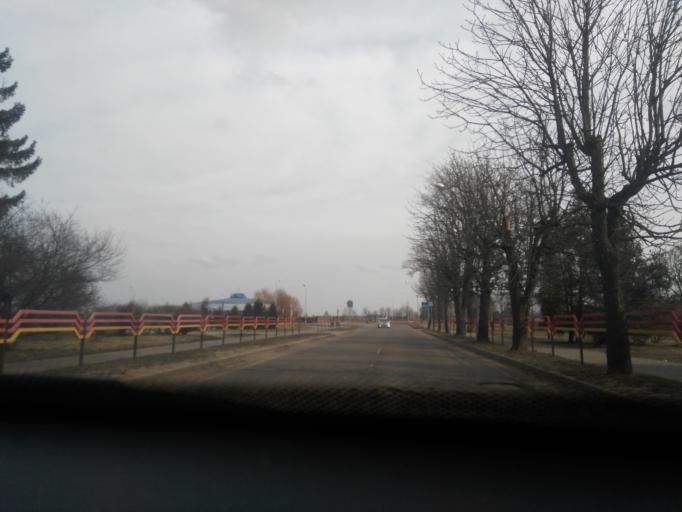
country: BY
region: Mogilev
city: Babruysk
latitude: 53.1437
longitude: 29.2383
